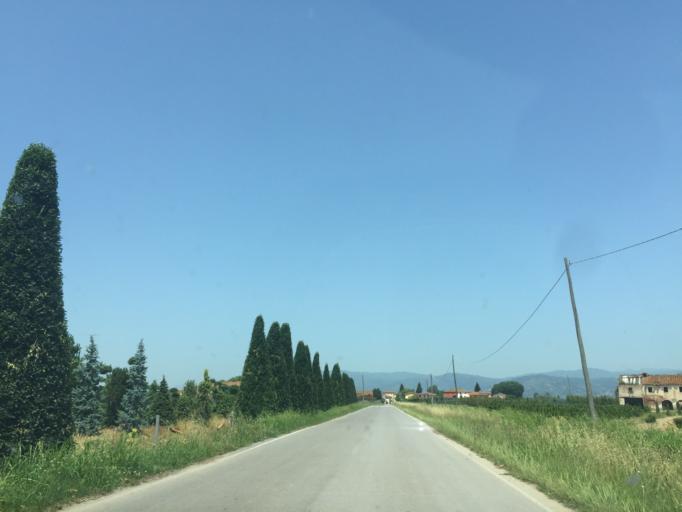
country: IT
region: Tuscany
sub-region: Provincia di Pistoia
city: Anchione
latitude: 43.8175
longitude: 10.7665
